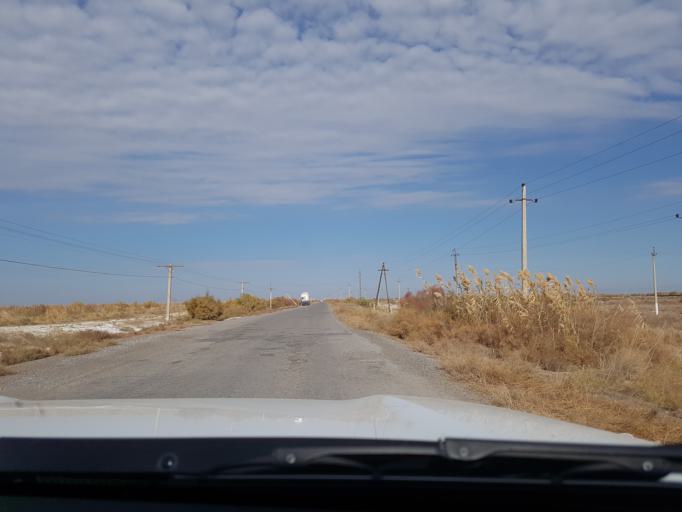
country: TM
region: Ahal
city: Tejen
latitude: 37.3422
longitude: 61.0912
